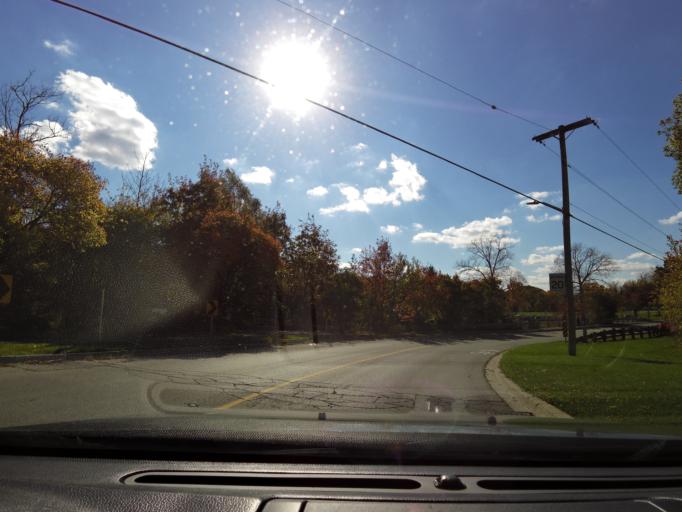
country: CA
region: Ontario
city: Hamilton
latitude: 43.3053
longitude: -79.8609
